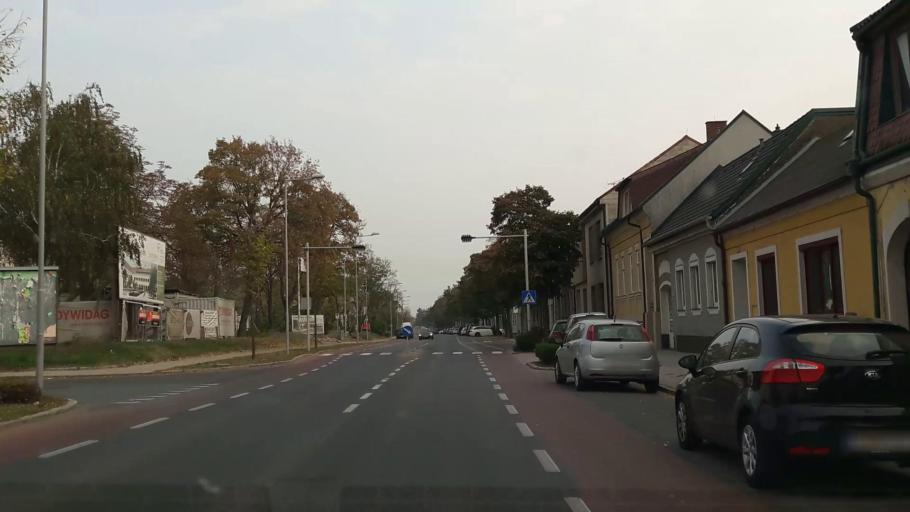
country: AT
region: Burgenland
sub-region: Politischer Bezirk Neusiedl am See
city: Neusiedl am See
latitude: 47.9424
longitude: 16.8507
